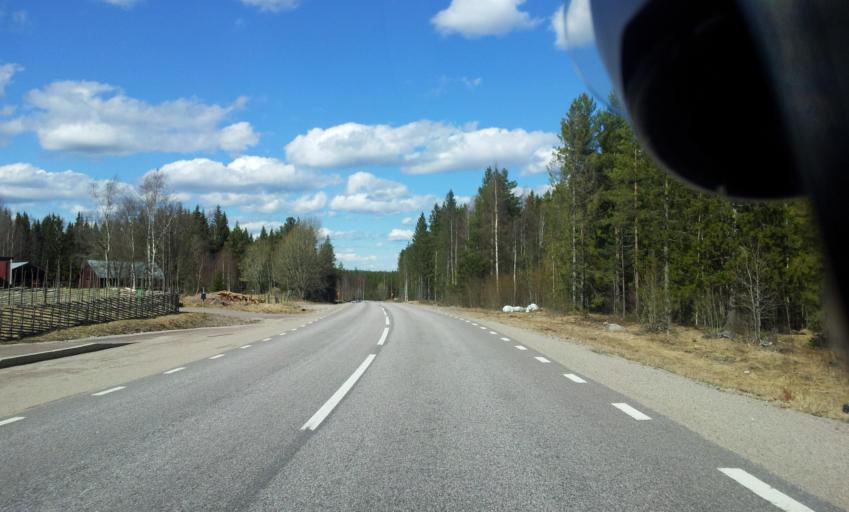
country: SE
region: Gaevleborg
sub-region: Bollnas Kommun
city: Vittsjo
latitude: 61.1425
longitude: 15.8867
